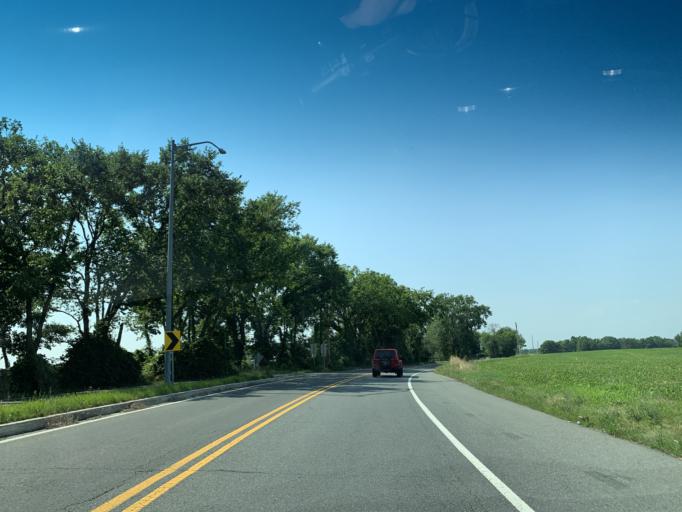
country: US
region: Maryland
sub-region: Montgomery County
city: Poolesville
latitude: 39.1284
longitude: -77.3836
